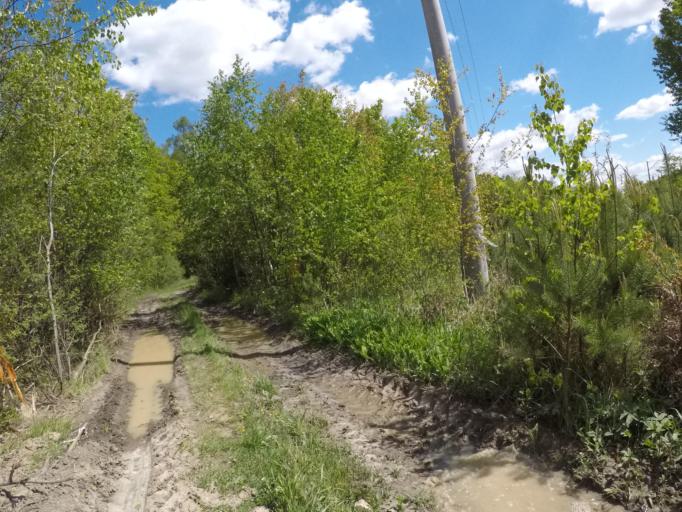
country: PL
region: Swietokrzyskie
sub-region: Powiat kielecki
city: Kostomloty Pierwsze
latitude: 50.9183
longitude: 20.6224
